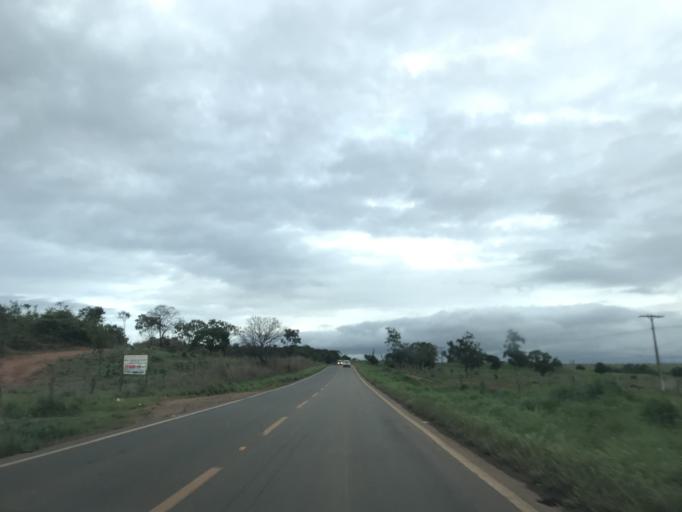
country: BR
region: Goias
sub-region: Luziania
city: Luziania
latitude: -16.2799
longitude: -47.9964
